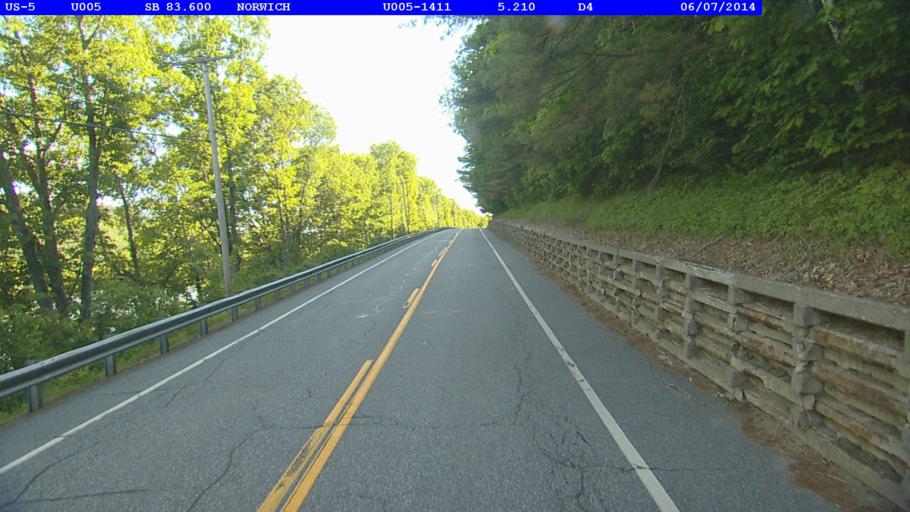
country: US
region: New Hampshire
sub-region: Grafton County
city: Hanover
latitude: 43.7419
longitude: -72.2487
